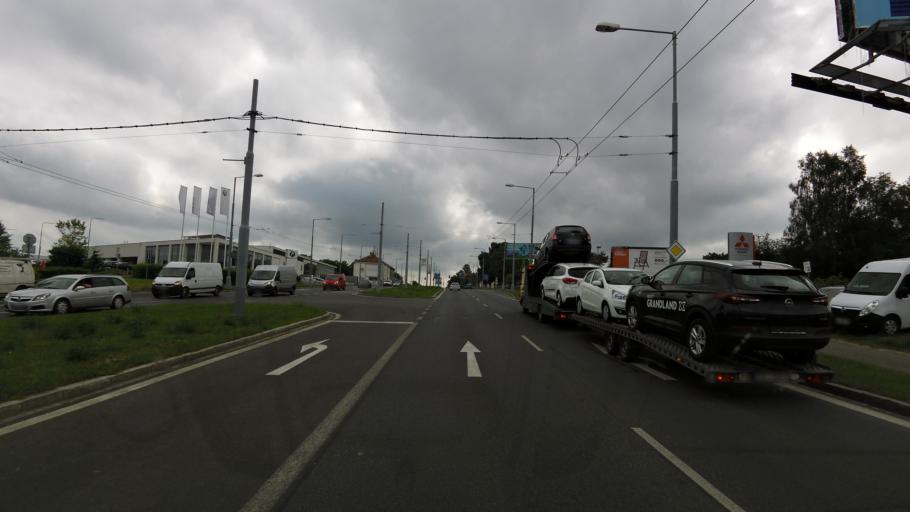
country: CZ
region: Plzensky
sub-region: Okres Plzen-Mesto
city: Pilsen
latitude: 49.7471
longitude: 13.4248
